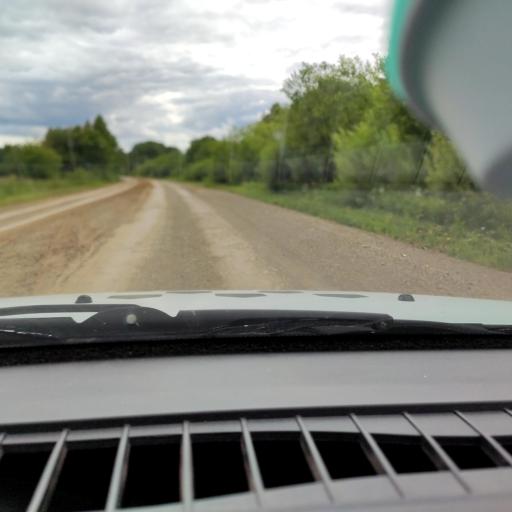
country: RU
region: Perm
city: Suksun
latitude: 57.1503
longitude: 57.5203
